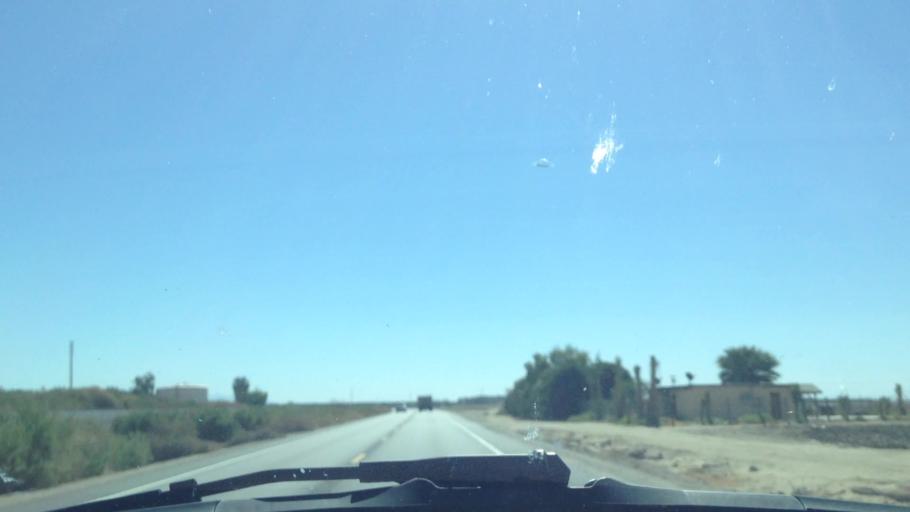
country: US
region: California
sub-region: Riverside County
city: Mecca
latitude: 33.5408
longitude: -116.0313
